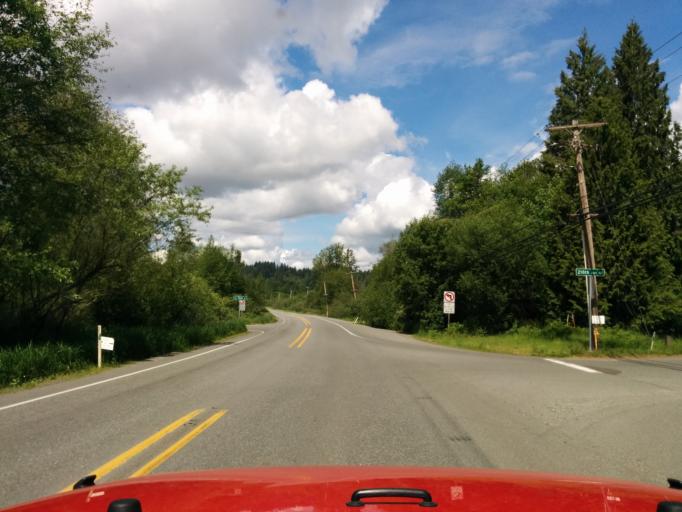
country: US
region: Washington
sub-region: King County
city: Sammamish
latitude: 47.6522
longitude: -122.0491
